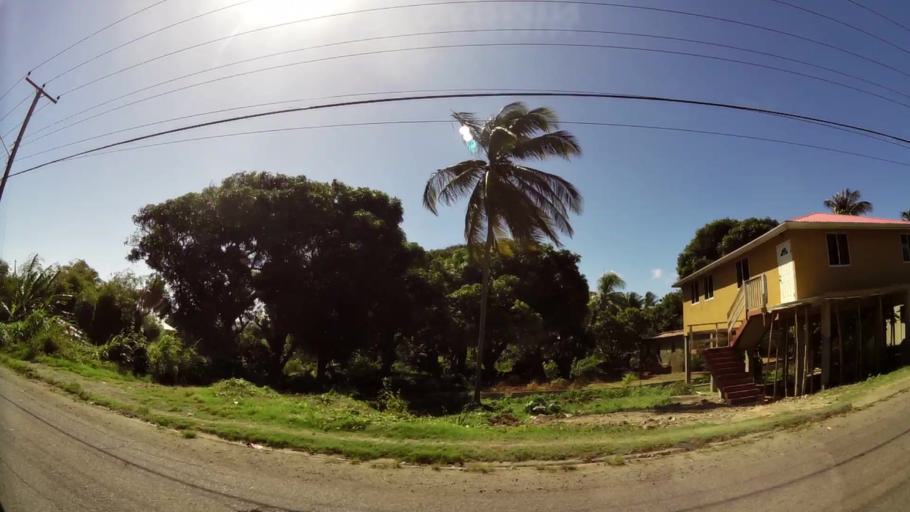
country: LC
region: Vieux-Fort
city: Vieux Fort
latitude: 13.7435
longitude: -60.9548
